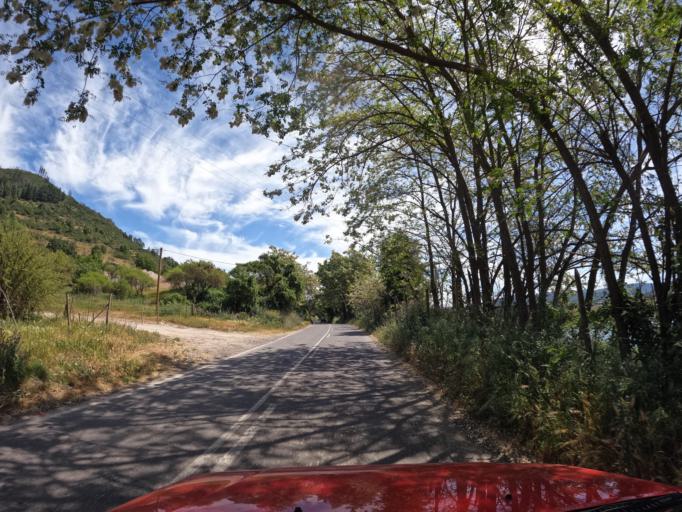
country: CL
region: Maule
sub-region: Provincia de Talca
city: Talca
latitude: -34.9888
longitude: -71.8294
